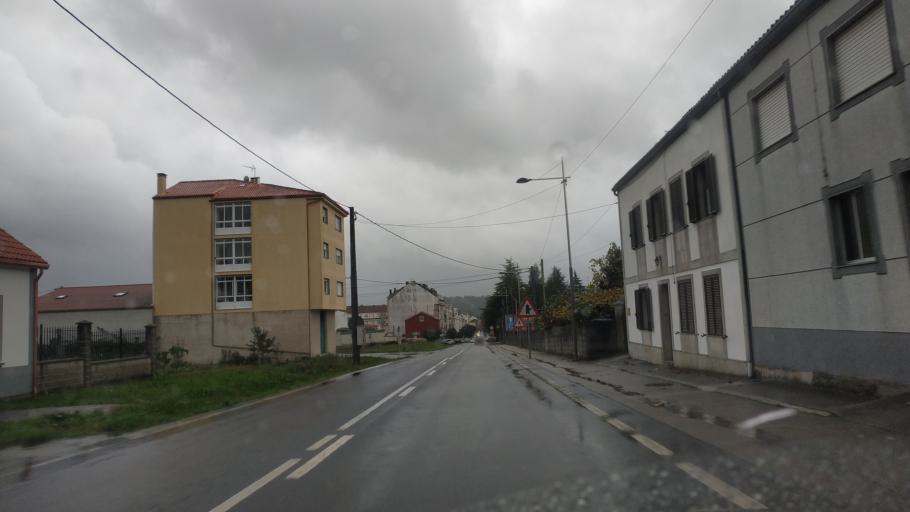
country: ES
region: Galicia
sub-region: Provincia da Coruna
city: Negreira
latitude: 42.9178
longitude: -8.7343
